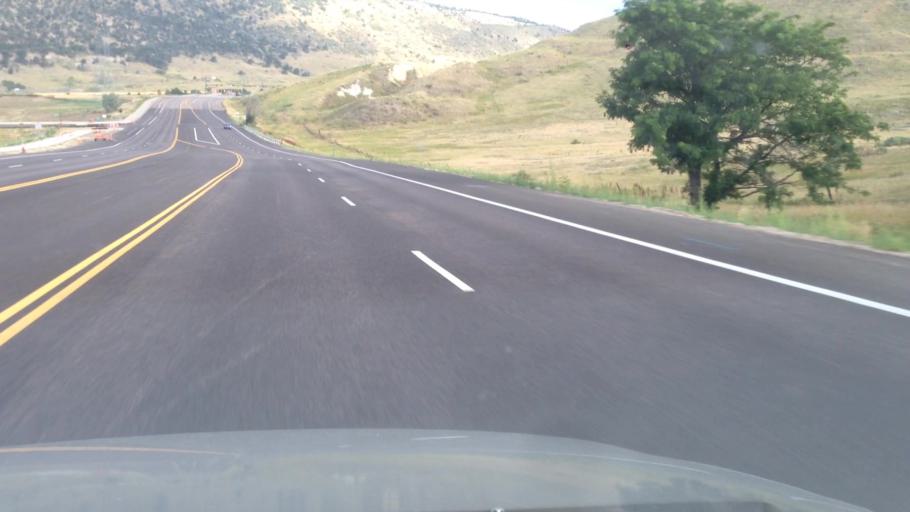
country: US
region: Colorado
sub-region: Jefferson County
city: West Pleasant View
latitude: 39.6837
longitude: -105.1802
